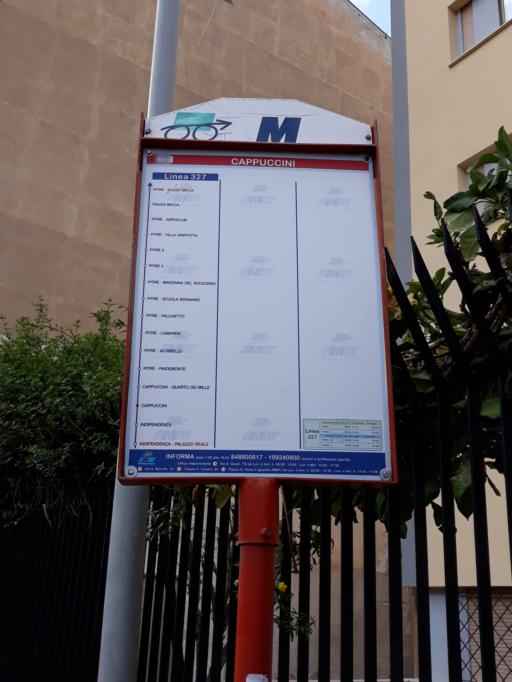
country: IT
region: Sicily
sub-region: Palermo
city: Palermo
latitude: 38.1105
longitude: 13.3469
